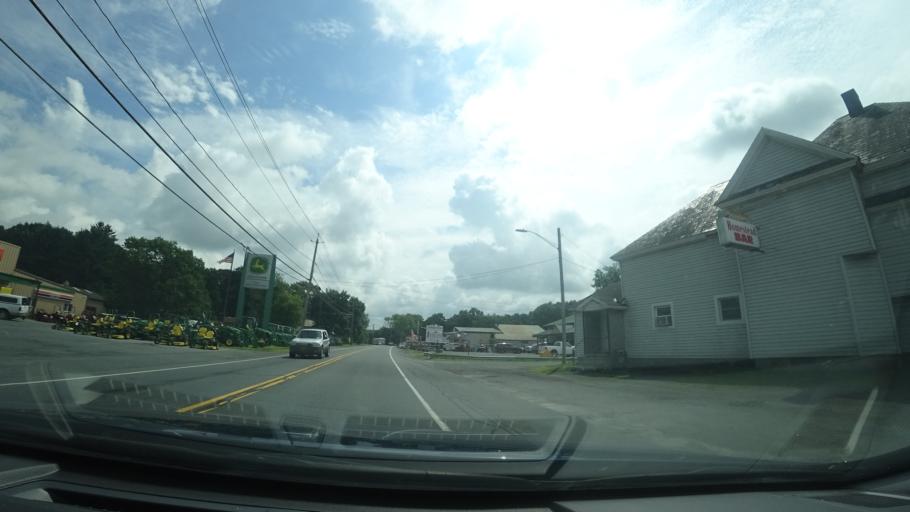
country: US
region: New York
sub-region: Washington County
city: Hudson Falls
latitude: 43.3196
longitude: -73.5871
